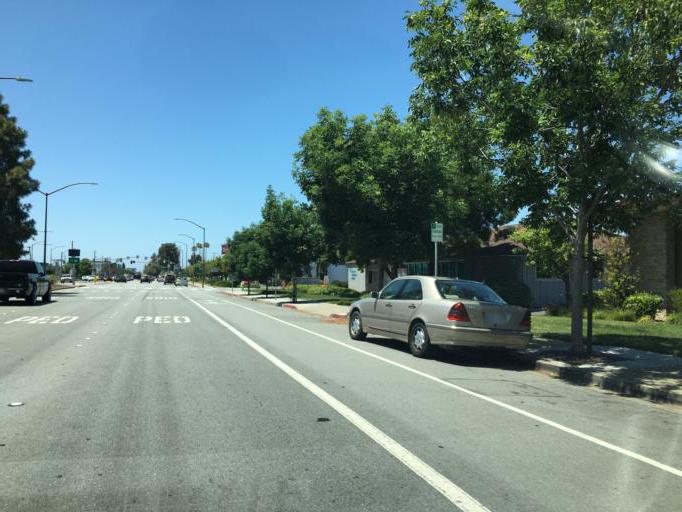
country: US
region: California
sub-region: San Mateo County
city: Redwood City
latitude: 37.4931
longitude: -122.2327
